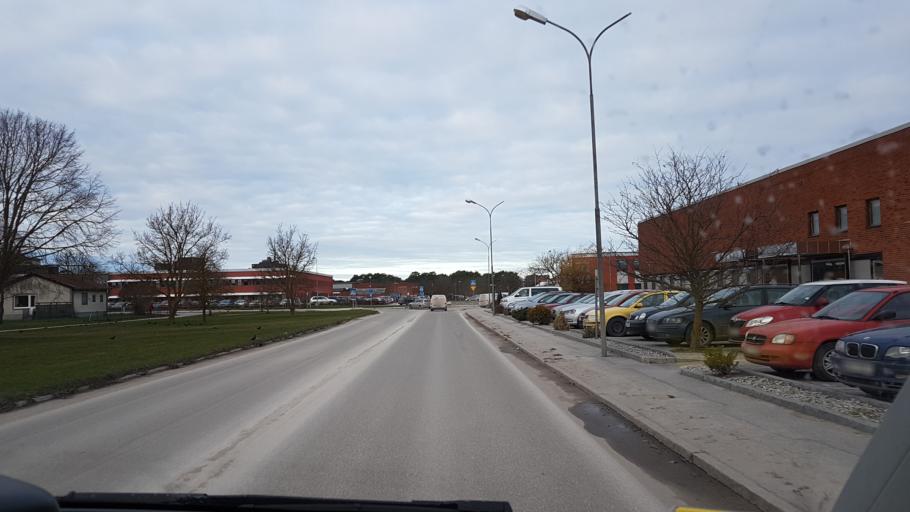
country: SE
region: Gotland
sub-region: Gotland
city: Visby
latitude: 57.6433
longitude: 18.3149
